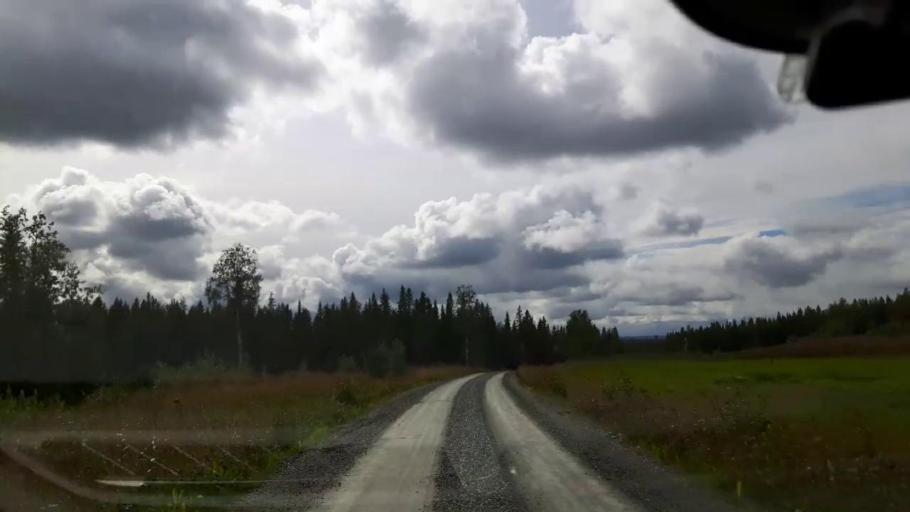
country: SE
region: Jaemtland
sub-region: Krokoms Kommun
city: Valla
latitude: 63.5765
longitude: 13.8965
